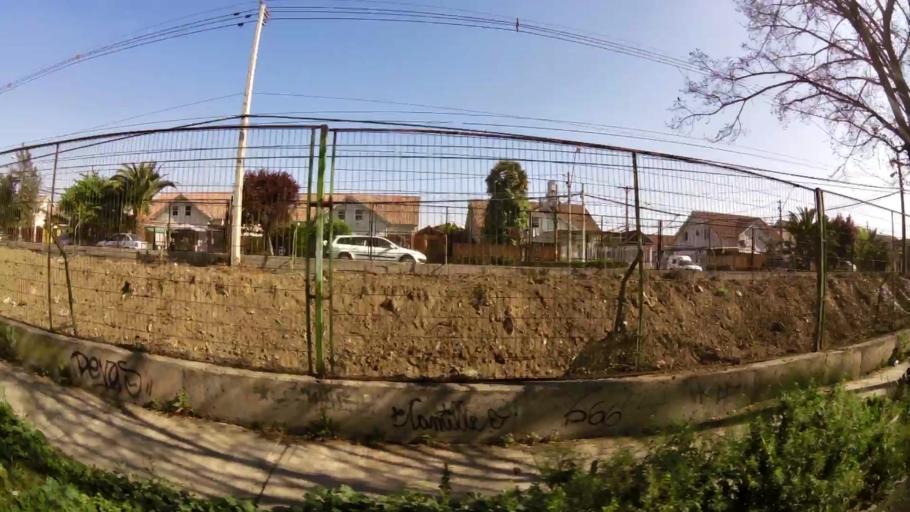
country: CL
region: Santiago Metropolitan
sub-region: Provincia de Santiago
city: Lo Prado
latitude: -33.4897
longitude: -70.7730
